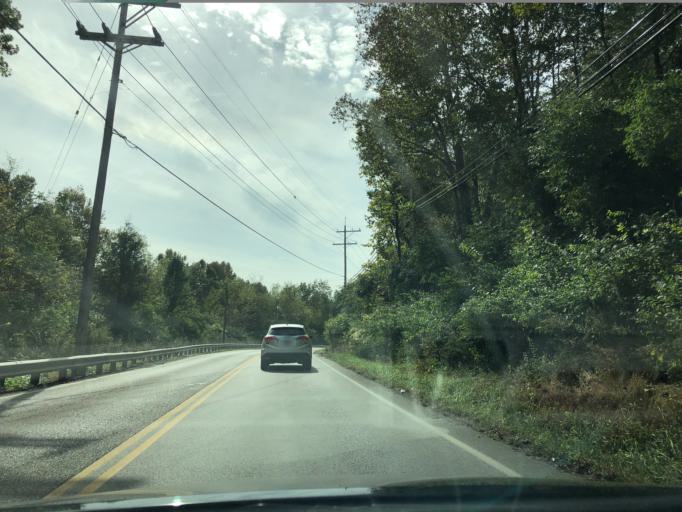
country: US
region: Ohio
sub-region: Clermont County
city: Milford
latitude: 39.1823
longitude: -84.2927
